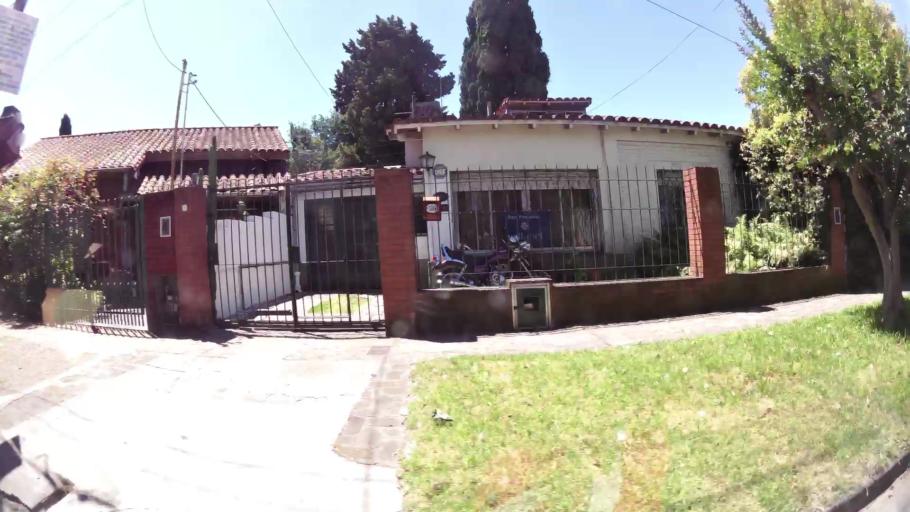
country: AR
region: Buenos Aires
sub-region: Partido de San Isidro
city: San Isidro
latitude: -34.5071
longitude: -58.5725
